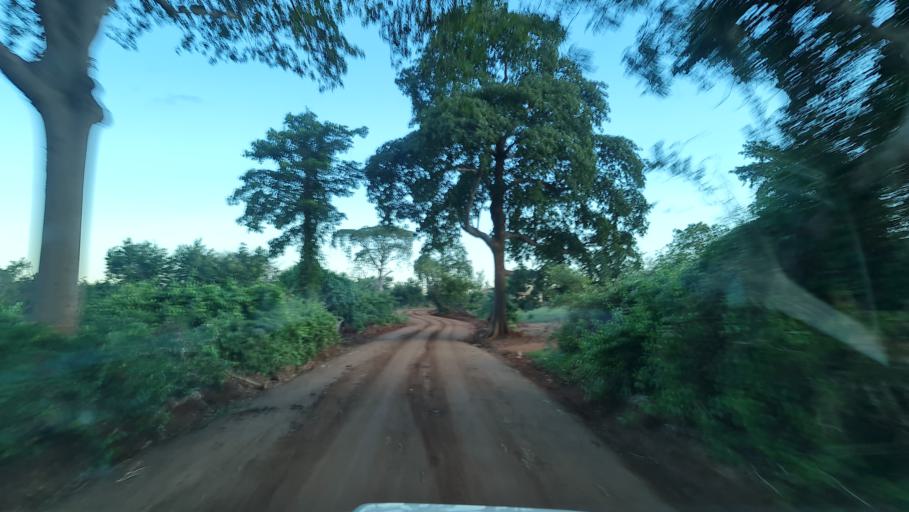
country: MZ
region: Nampula
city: Ilha de Mocambique
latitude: -14.9812
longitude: 40.0940
